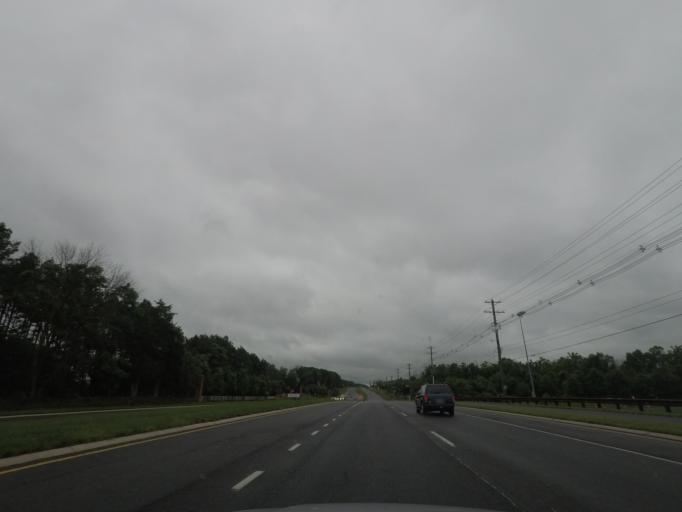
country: US
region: Virginia
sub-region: Prince William County
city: Haymarket
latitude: 38.8559
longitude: -77.6378
